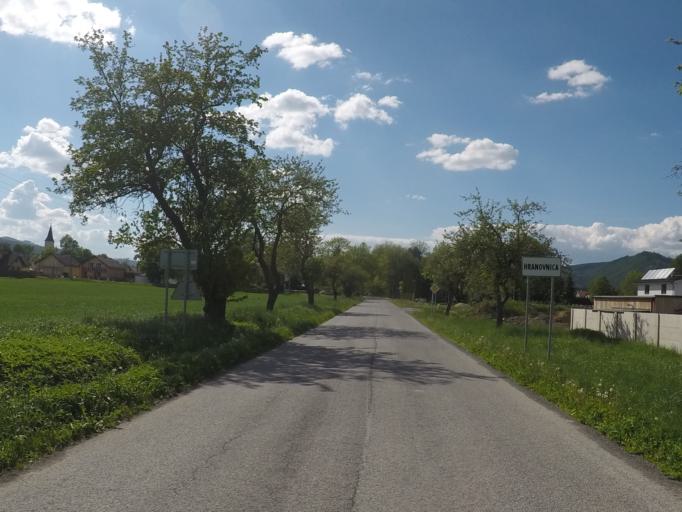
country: SK
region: Presovsky
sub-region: Okres Poprad
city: Poprad
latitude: 48.9901
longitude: 20.3143
